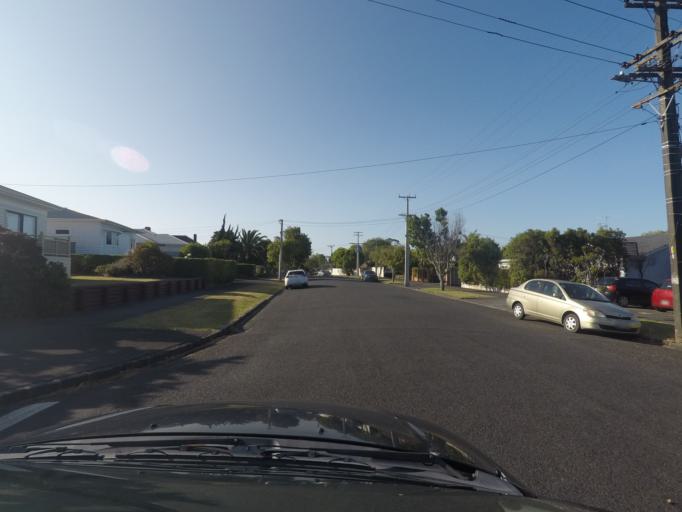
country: NZ
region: Auckland
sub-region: Auckland
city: Rosebank
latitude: -36.8656
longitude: 174.7160
